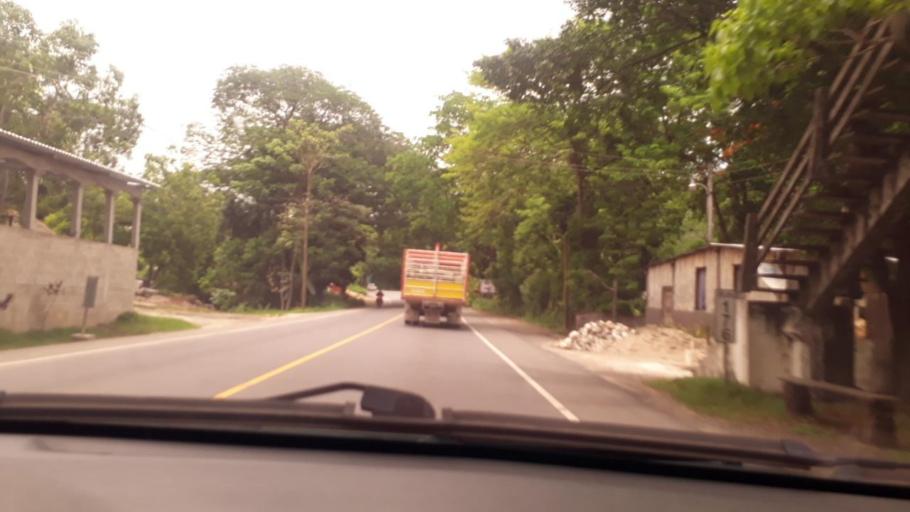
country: GT
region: Zacapa
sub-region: Municipio de Zacapa
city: Gualan
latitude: 15.1847
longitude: -89.2863
